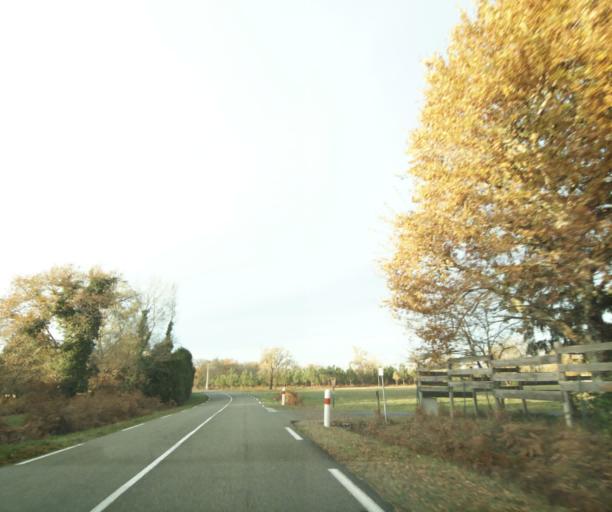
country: FR
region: Aquitaine
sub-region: Departement des Landes
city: Gabarret
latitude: 44.0963
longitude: -0.0995
